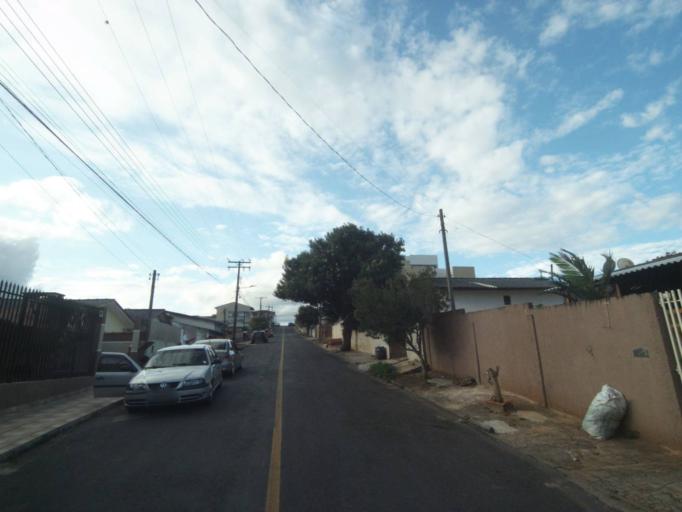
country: BR
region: Parana
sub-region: Telemaco Borba
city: Telemaco Borba
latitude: -24.3246
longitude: -50.6376
